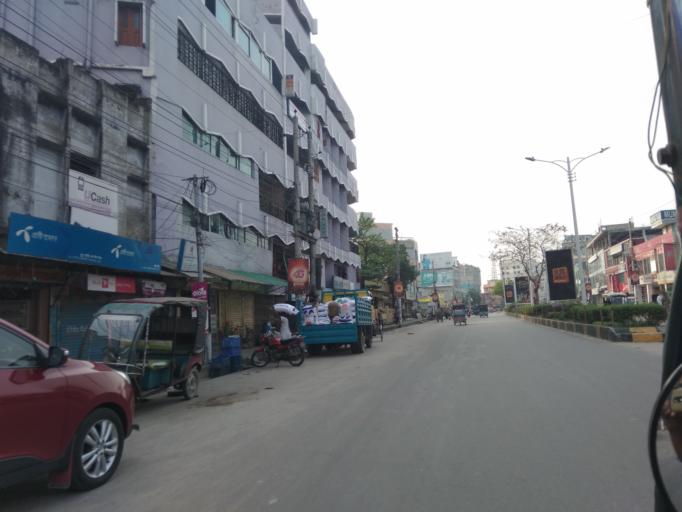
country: BD
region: Khulna
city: Khulna
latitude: 22.8136
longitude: 89.5560
